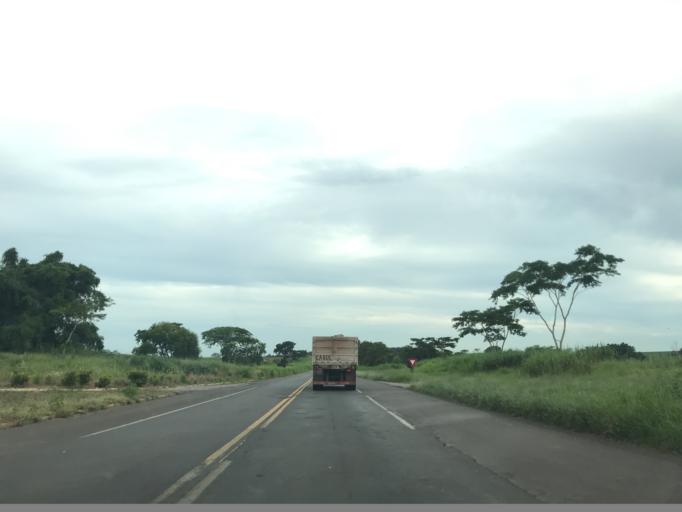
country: BR
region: Sao Paulo
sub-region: Tupa
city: Tupa
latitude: -21.6552
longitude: -50.5338
